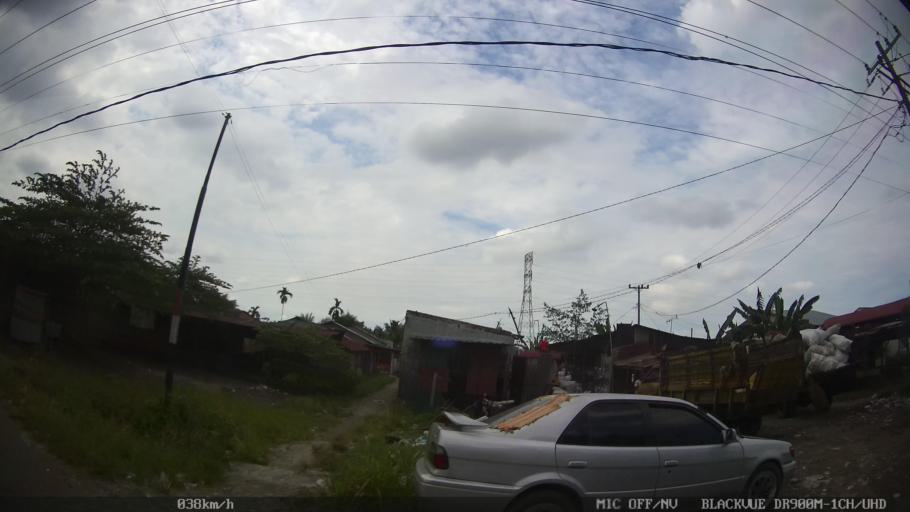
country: ID
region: North Sumatra
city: Sunggal
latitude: 3.6180
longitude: 98.6214
